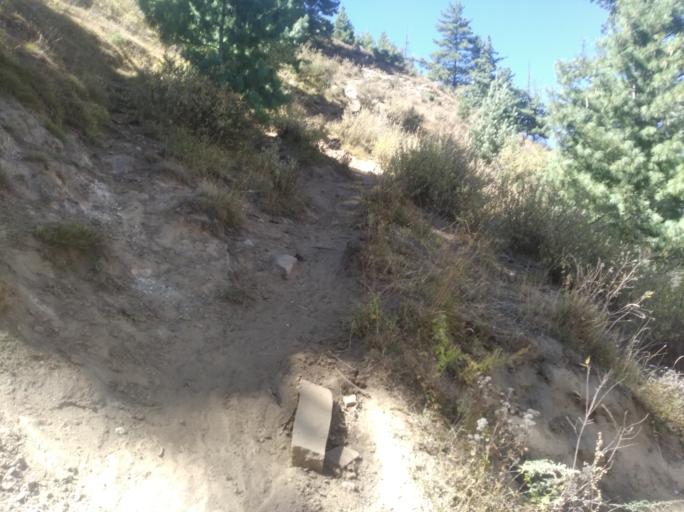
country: NP
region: Western Region
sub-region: Dhawalagiri Zone
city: Jomsom
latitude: 28.8890
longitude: 83.0694
